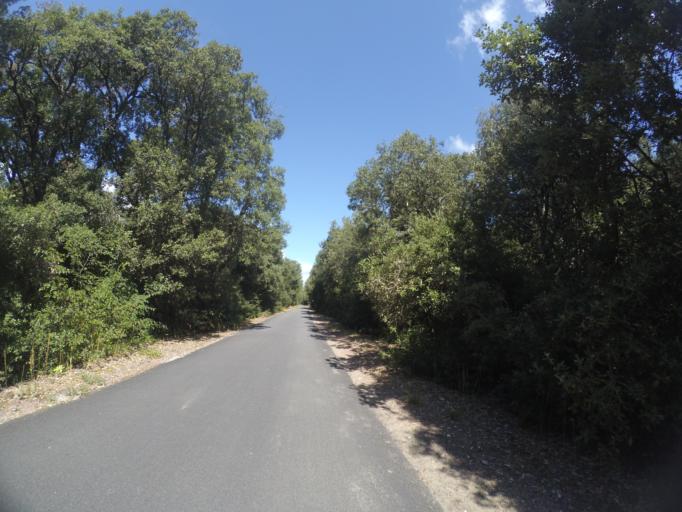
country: FR
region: Poitou-Charentes
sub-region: Departement de la Charente-Maritime
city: Les Mathes
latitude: 45.6732
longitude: -1.1494
